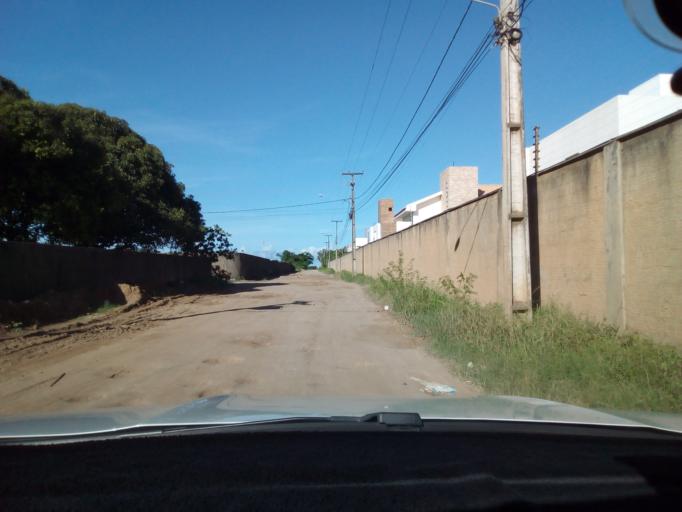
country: BR
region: Paraiba
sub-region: Joao Pessoa
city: Joao Pessoa
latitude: -7.1523
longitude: -34.8157
